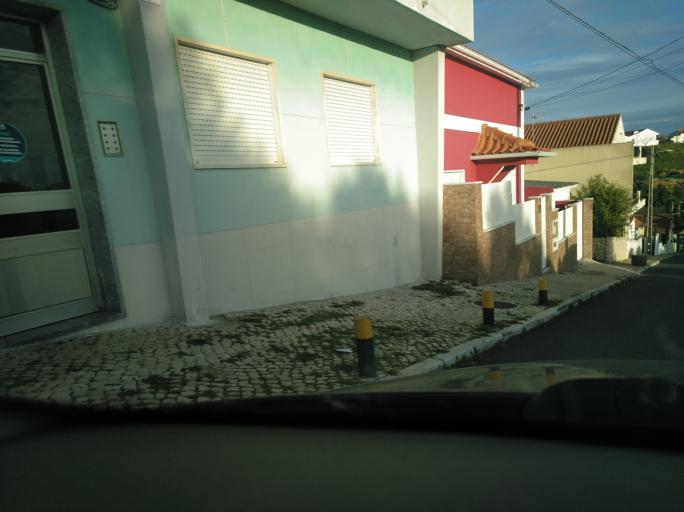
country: PT
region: Lisbon
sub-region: Loures
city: Apelacao
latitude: 38.8135
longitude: -9.1205
